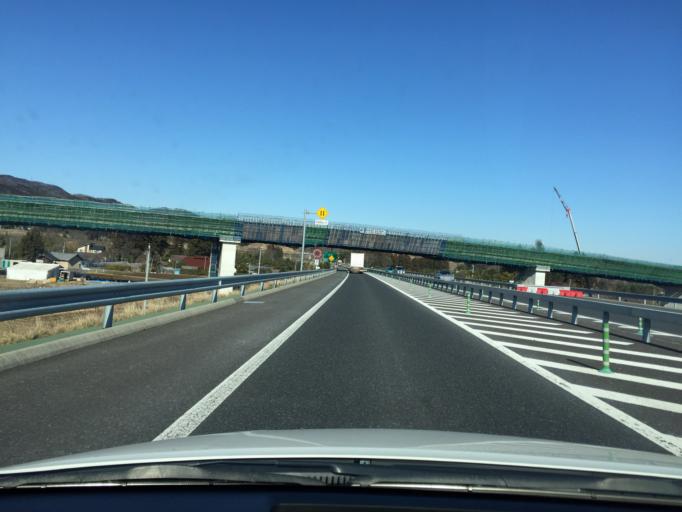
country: JP
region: Miyagi
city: Marumori
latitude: 37.7741
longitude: 140.8992
